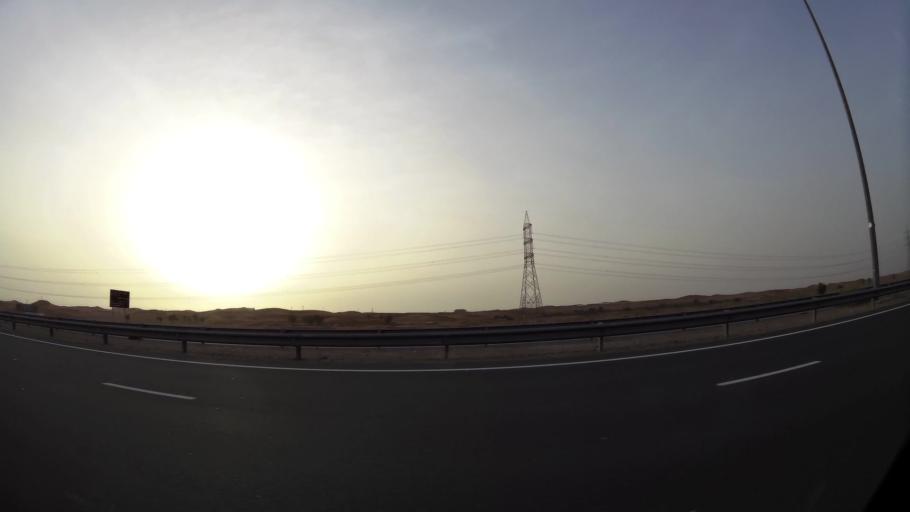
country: OM
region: Al Buraimi
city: Al Buraymi
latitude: 24.3348
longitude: 55.7673
